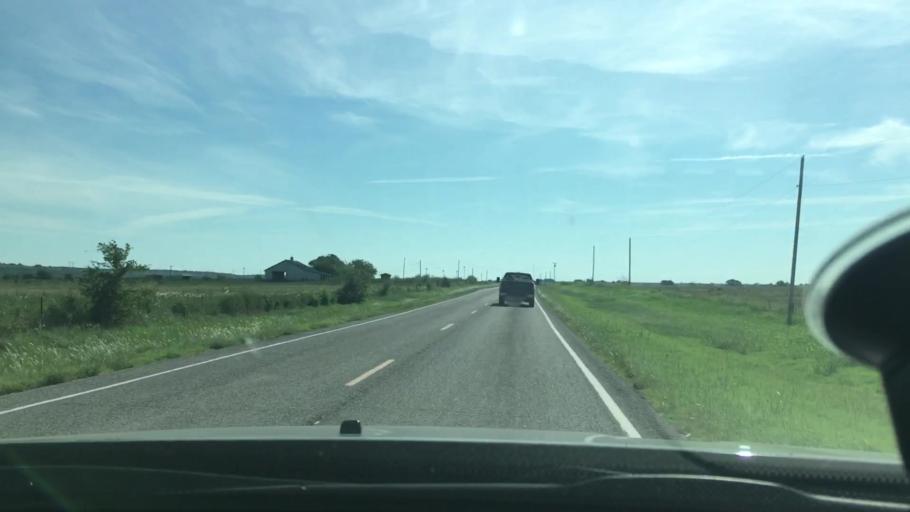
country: US
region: Oklahoma
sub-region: Carter County
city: Lone Grove
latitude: 34.3327
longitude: -97.2544
